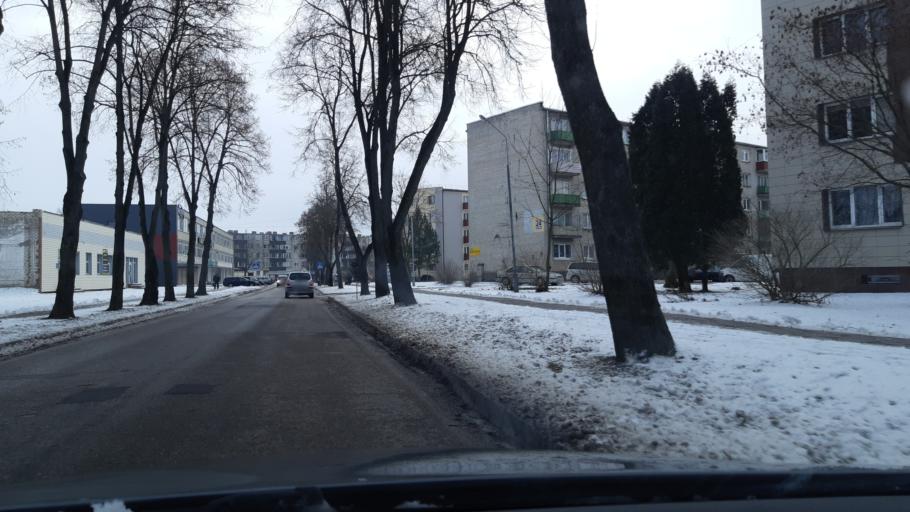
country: LT
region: Kauno apskritis
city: Kedainiai
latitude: 55.2913
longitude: 23.9814
